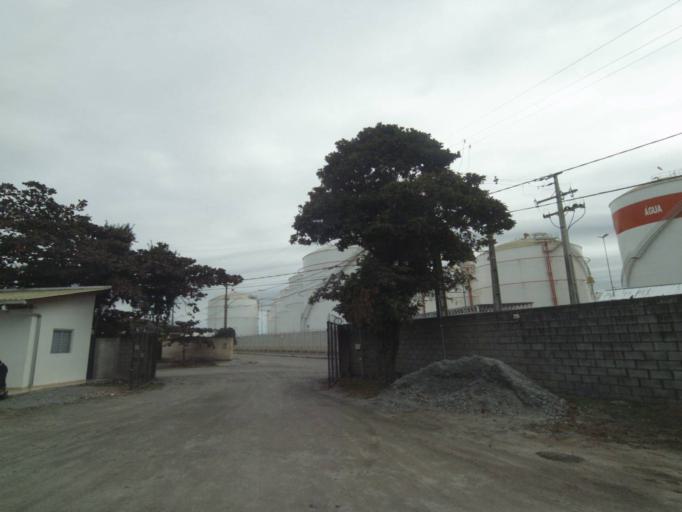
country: BR
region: Parana
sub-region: Paranagua
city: Paranagua
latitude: -25.5140
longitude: -48.5285
